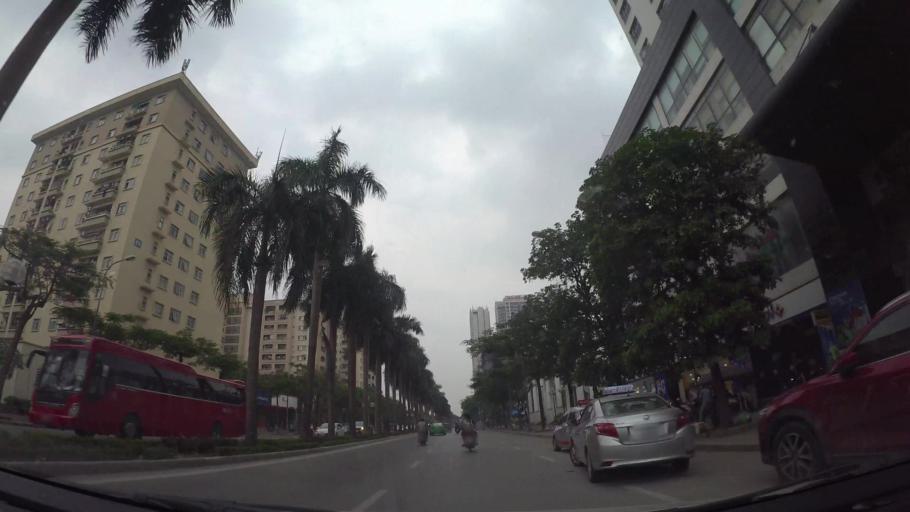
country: VN
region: Ha Noi
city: Cau Dien
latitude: 21.0301
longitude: 105.7692
